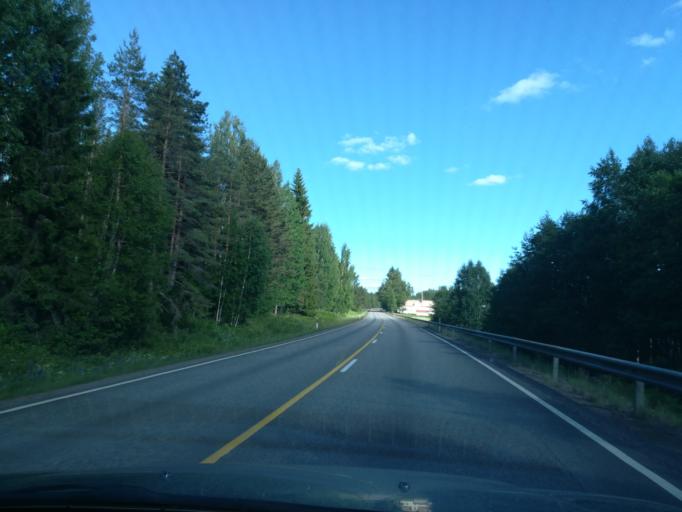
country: FI
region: South Karelia
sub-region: Imatra
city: Ruokolahti
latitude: 61.3736
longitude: 28.6627
